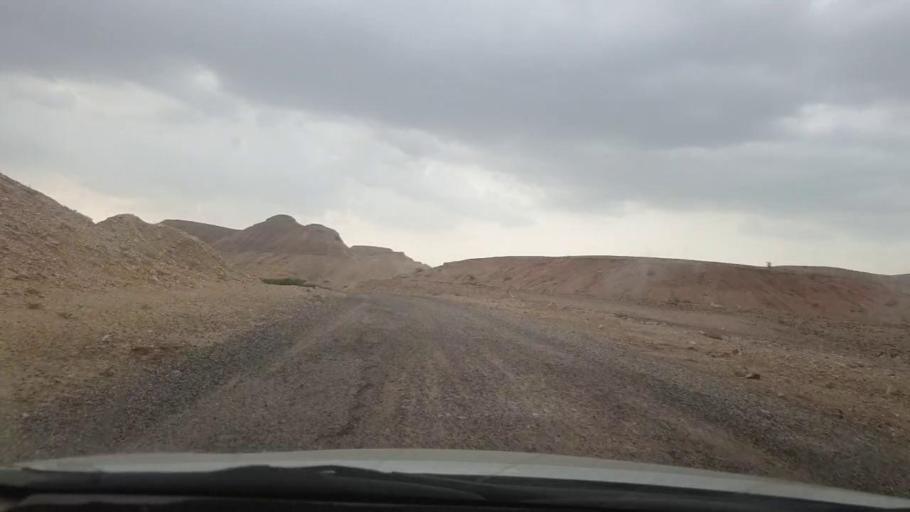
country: PK
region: Sindh
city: Khairpur
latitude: 27.4706
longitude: 68.9156
